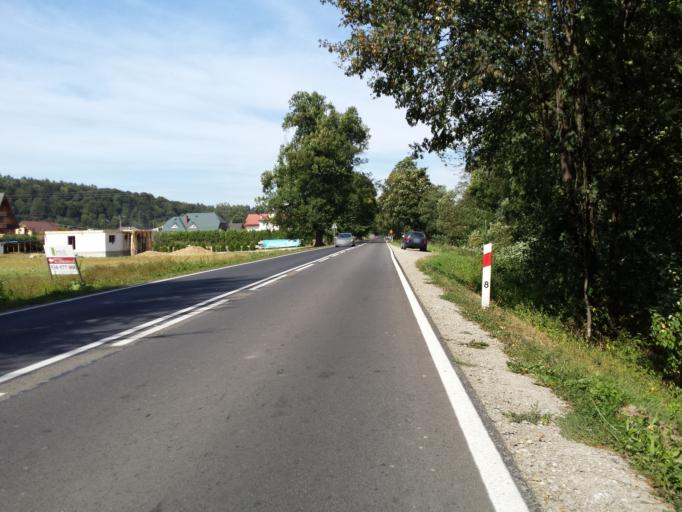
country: PL
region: Subcarpathian Voivodeship
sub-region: Powiat leski
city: Lesko
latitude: 49.4565
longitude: 22.3403
